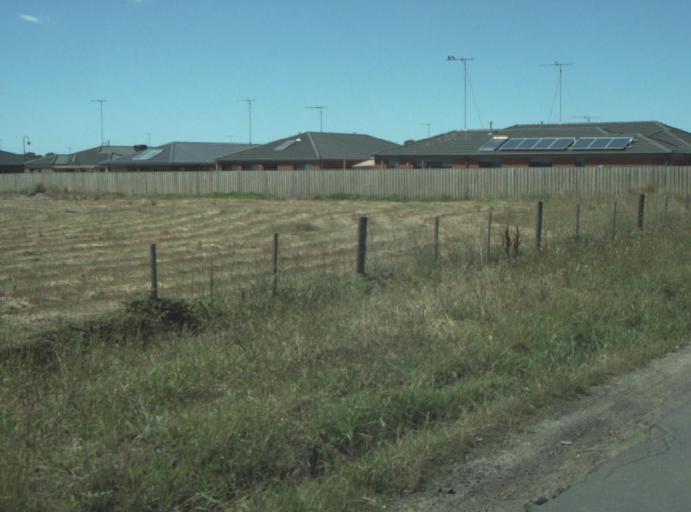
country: AU
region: Victoria
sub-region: Greater Geelong
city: Breakwater
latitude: -38.1899
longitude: 144.3538
